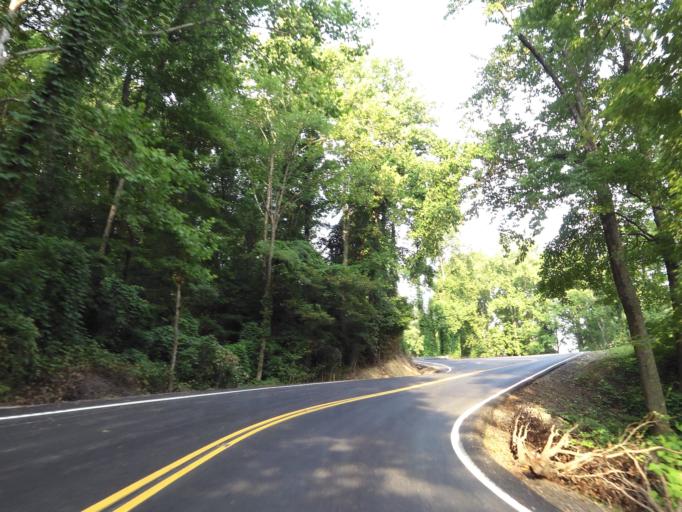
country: US
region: Tennessee
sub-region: Morgan County
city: Coalfield
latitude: 36.1043
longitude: -84.4469
